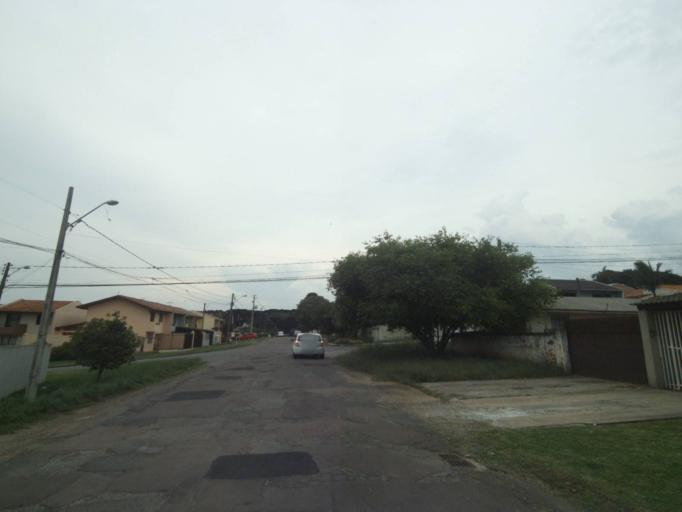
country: BR
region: Parana
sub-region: Pinhais
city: Pinhais
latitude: -25.3978
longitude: -49.2006
